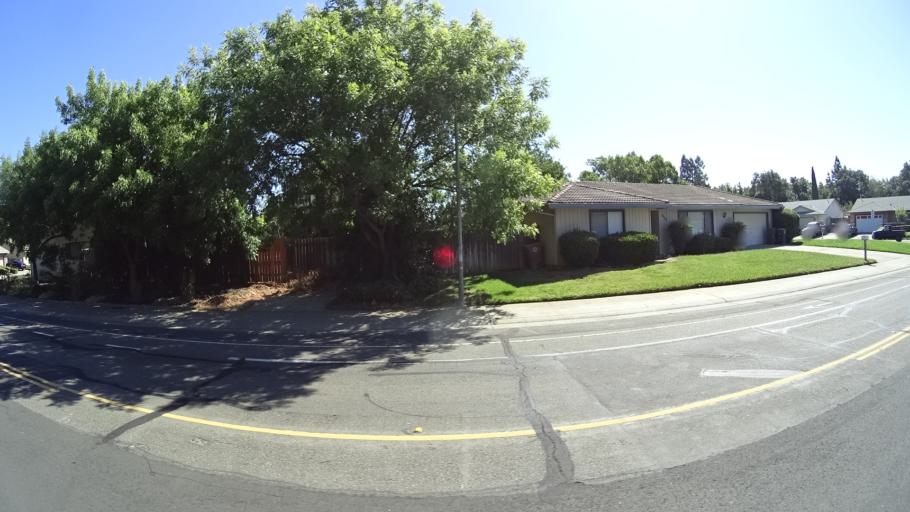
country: US
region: California
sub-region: Sacramento County
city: Elk Grove
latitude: 38.4119
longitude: -121.3837
